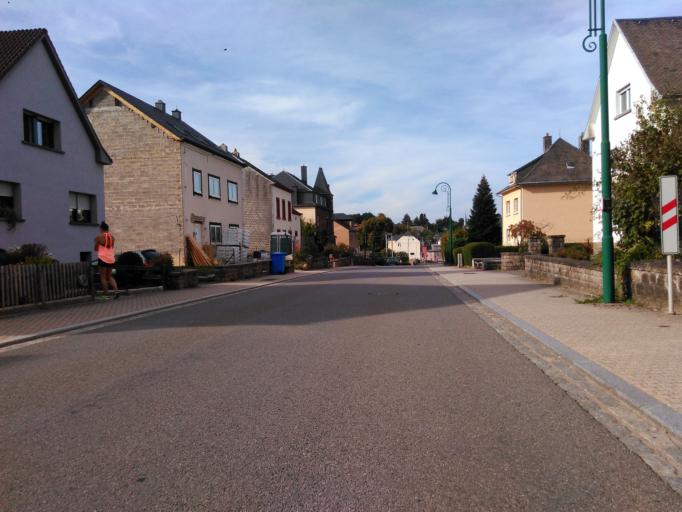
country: LU
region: Luxembourg
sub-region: Canton de Capellen
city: Steinfort
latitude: 49.6423
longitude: 5.9156
